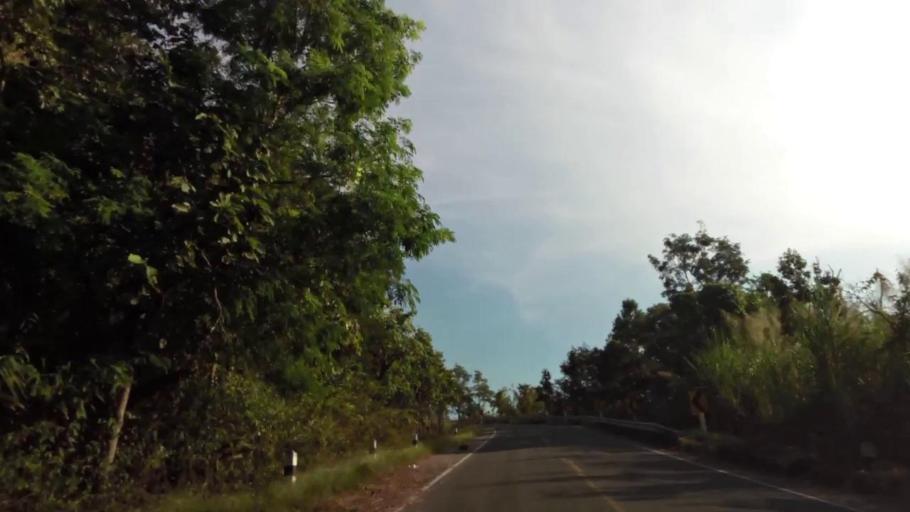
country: TH
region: Chiang Rai
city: Khun Tan
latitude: 19.8771
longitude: 100.3146
